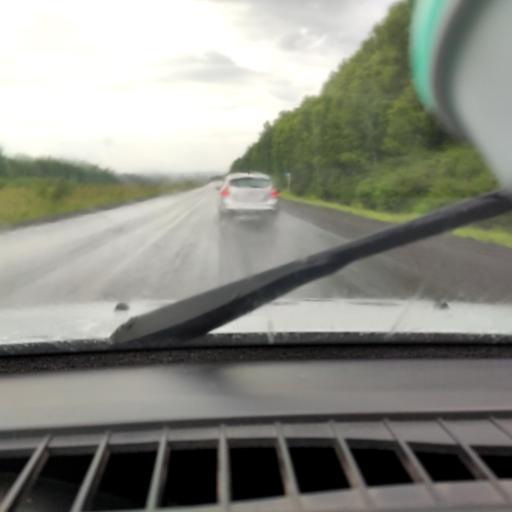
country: RU
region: Sverdlovsk
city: Achit
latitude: 56.7351
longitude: 57.8395
